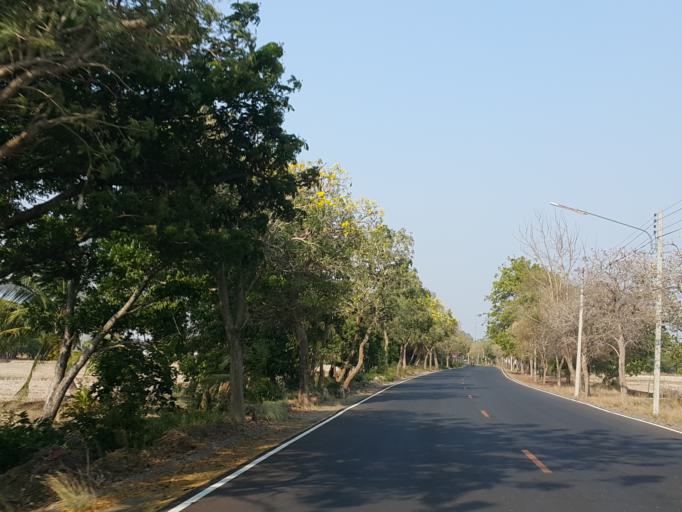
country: TH
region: Suphan Buri
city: Sam Chuk
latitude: 14.7518
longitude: 100.0635
